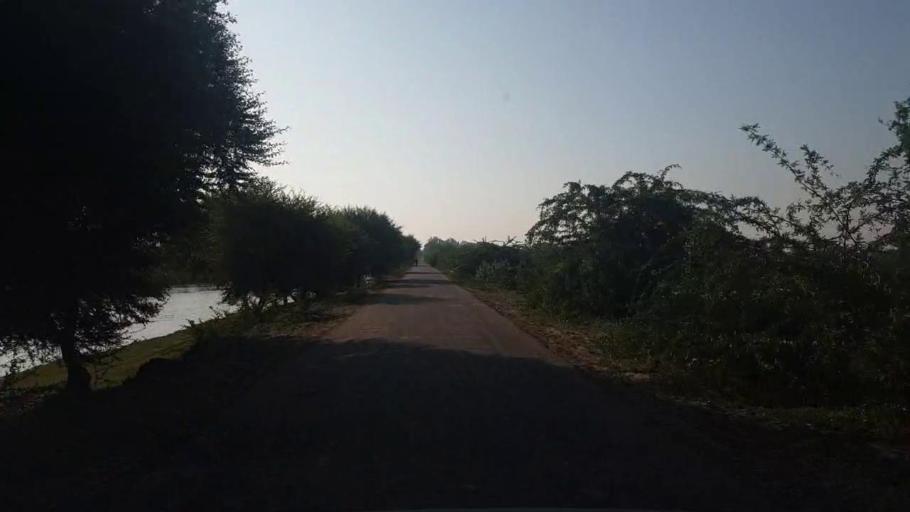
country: PK
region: Sindh
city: Tando Bago
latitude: 24.7297
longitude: 68.9366
